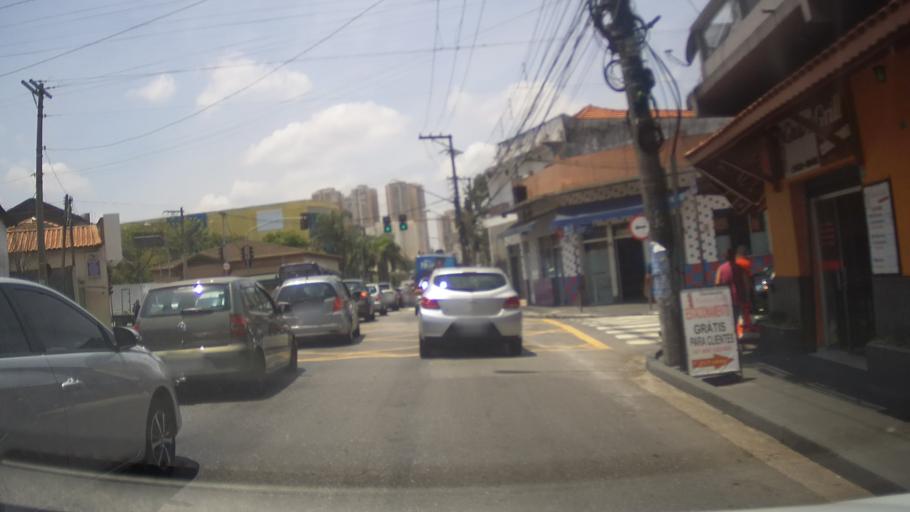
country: BR
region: Sao Paulo
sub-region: Guarulhos
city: Guarulhos
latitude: -23.4909
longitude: -46.5459
